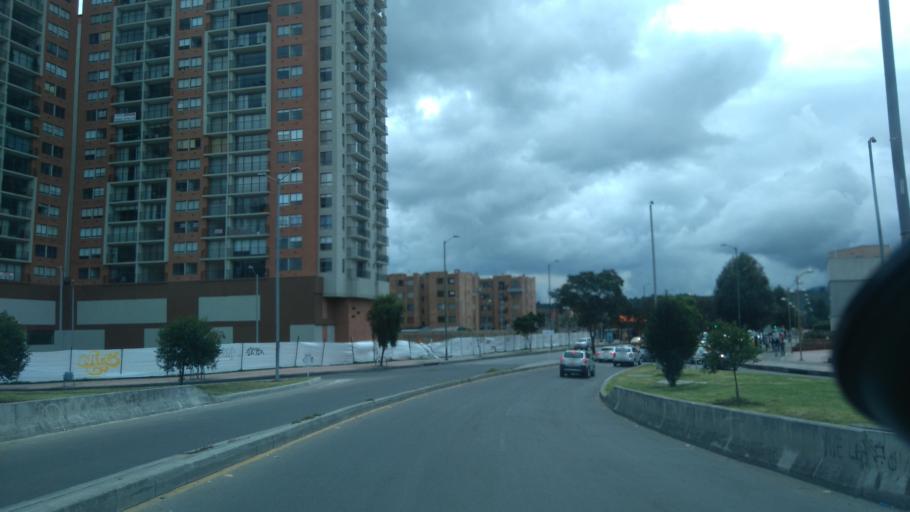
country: CO
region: Cundinamarca
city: Cota
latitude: 4.7605
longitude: -74.0462
